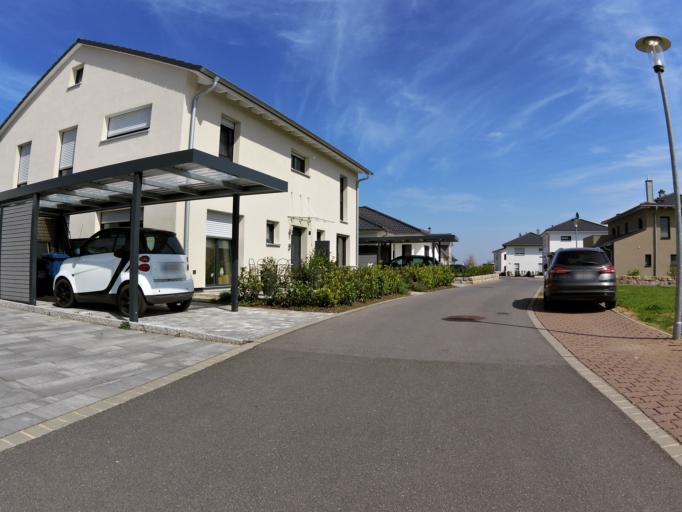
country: DE
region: Bavaria
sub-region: Regierungsbezirk Unterfranken
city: Unterpleichfeld
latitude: 49.8722
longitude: 10.0435
